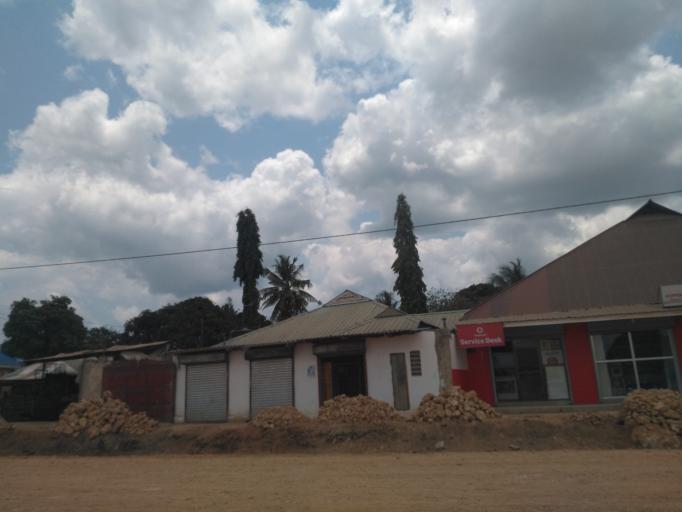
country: TZ
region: Dar es Salaam
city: Dar es Salaam
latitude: -6.8418
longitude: 39.3197
